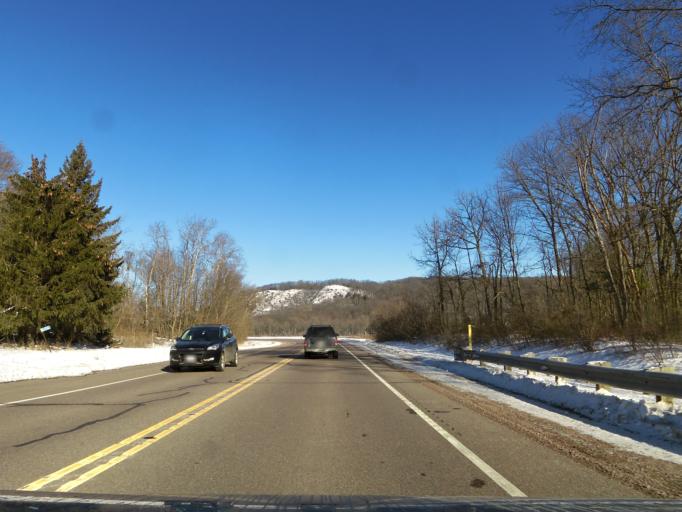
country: US
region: Wisconsin
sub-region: Sauk County
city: Baraboo
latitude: 43.4908
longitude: -89.6364
